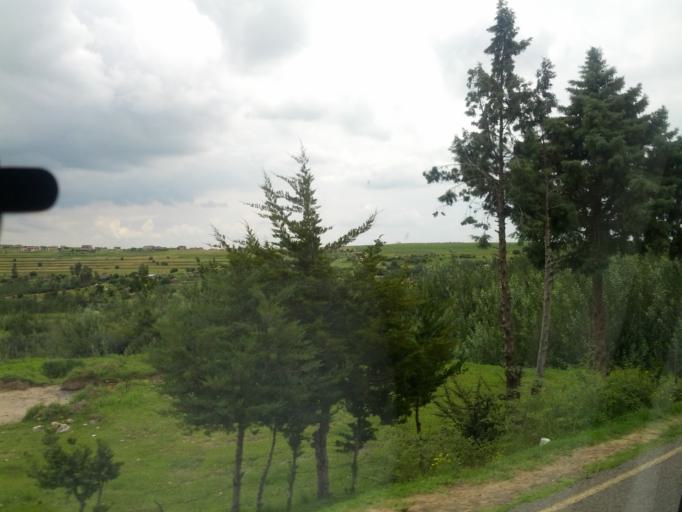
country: LS
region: Leribe
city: Leribe
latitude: -28.9569
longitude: 28.1729
